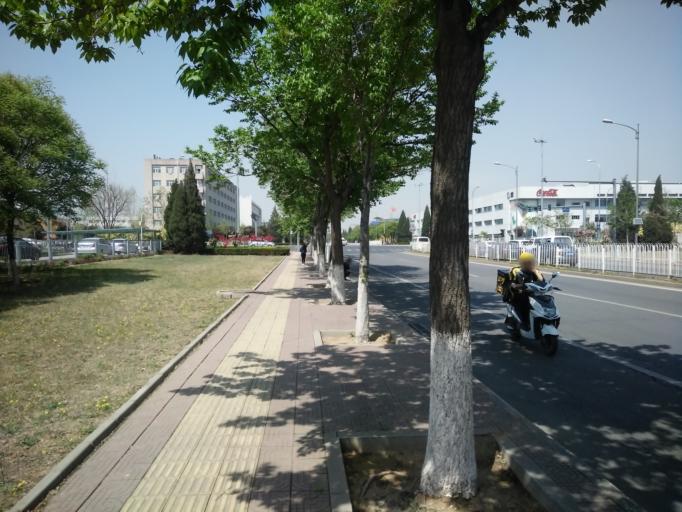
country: CN
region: Beijing
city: Jiugong
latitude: 39.7943
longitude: 116.5113
